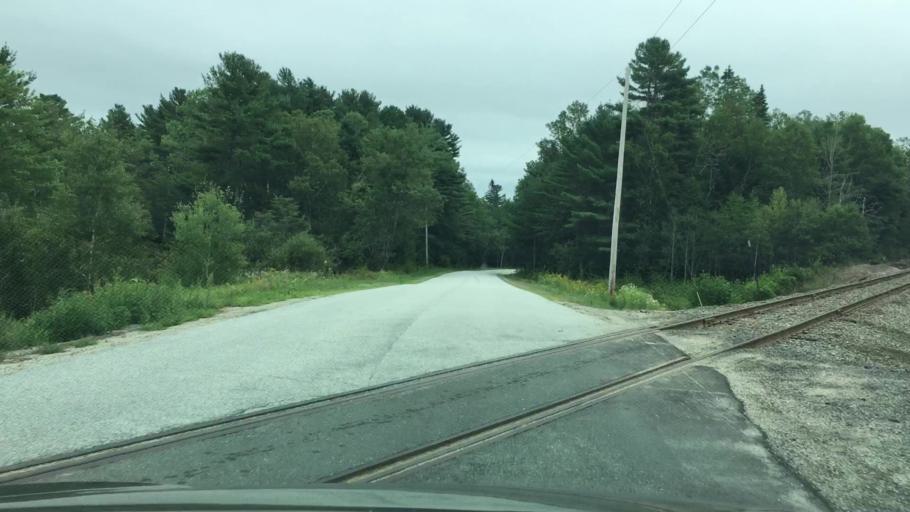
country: US
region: Maine
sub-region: Waldo County
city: Stockton Springs
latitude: 44.5296
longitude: -68.8340
